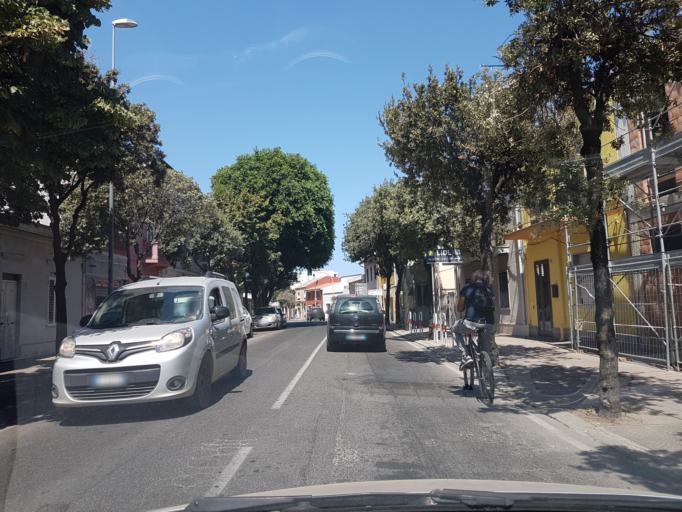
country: IT
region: Sardinia
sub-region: Provincia di Oristano
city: Oristano
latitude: 39.8981
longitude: 8.5945
